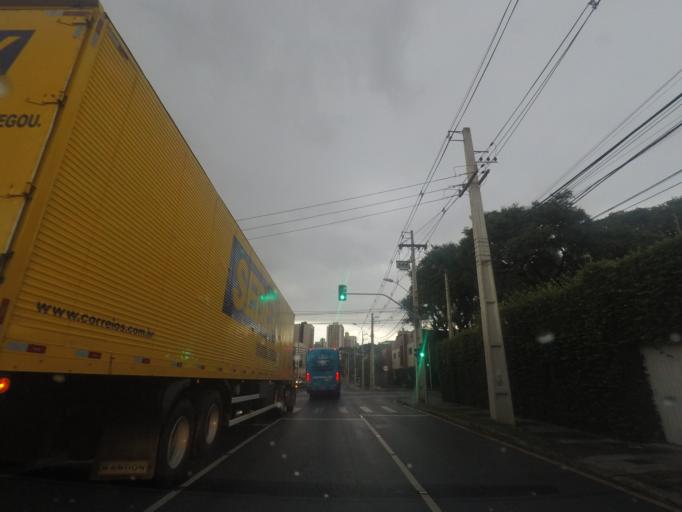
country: BR
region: Parana
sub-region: Curitiba
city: Curitiba
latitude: -25.4395
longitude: -49.2524
